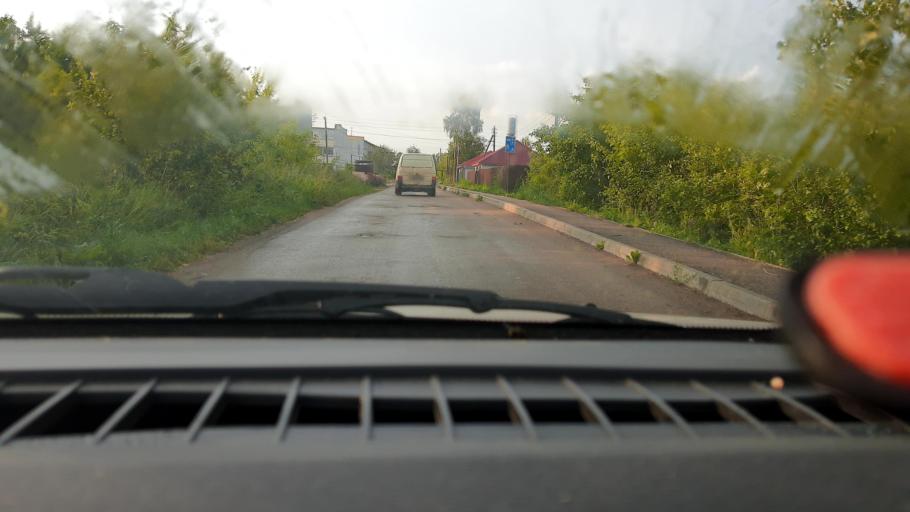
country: RU
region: Nizjnij Novgorod
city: Lukoyanov
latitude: 55.0427
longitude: 44.4939
